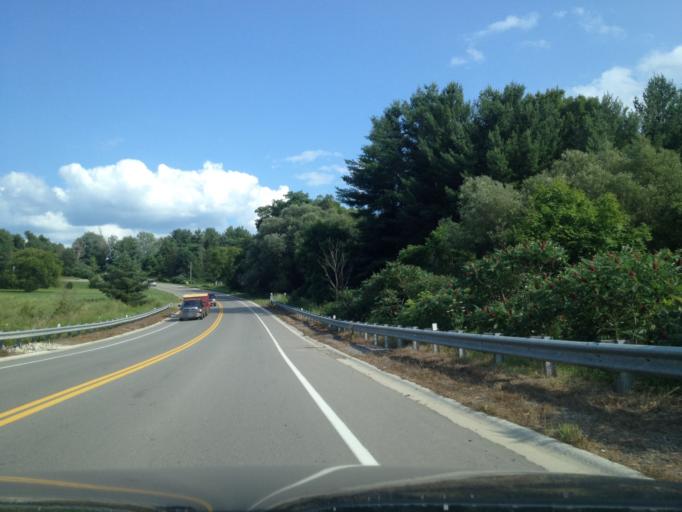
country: CA
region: Ontario
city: Aylmer
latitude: 42.7613
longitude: -80.8404
